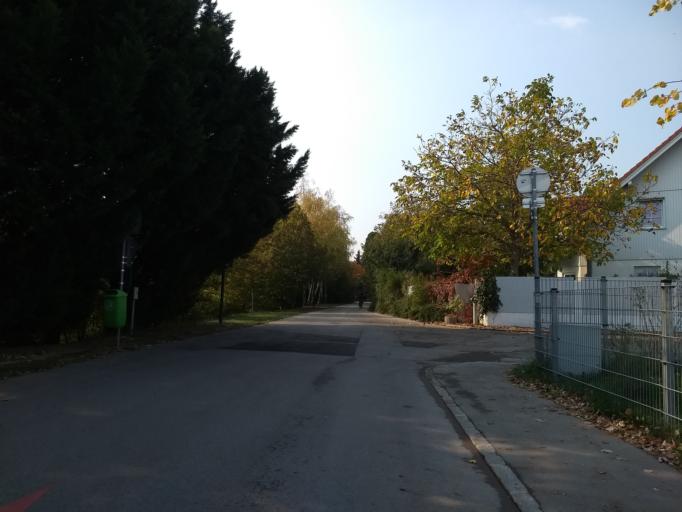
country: AT
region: Lower Austria
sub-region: Politischer Bezirk Modling
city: Brunn am Gebirge
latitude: 48.1257
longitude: 16.2913
